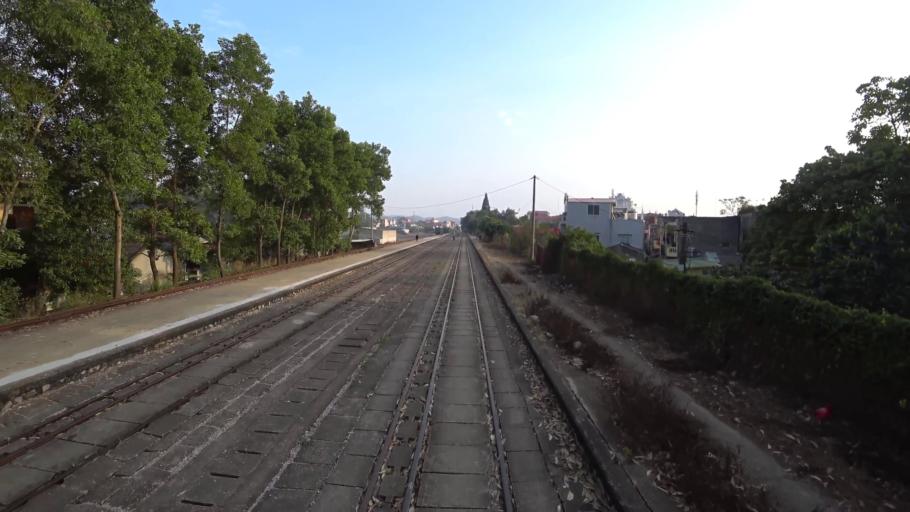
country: VN
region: Lang Son
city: Thi Tran Cao Loc
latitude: 21.8676
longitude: 106.7627
